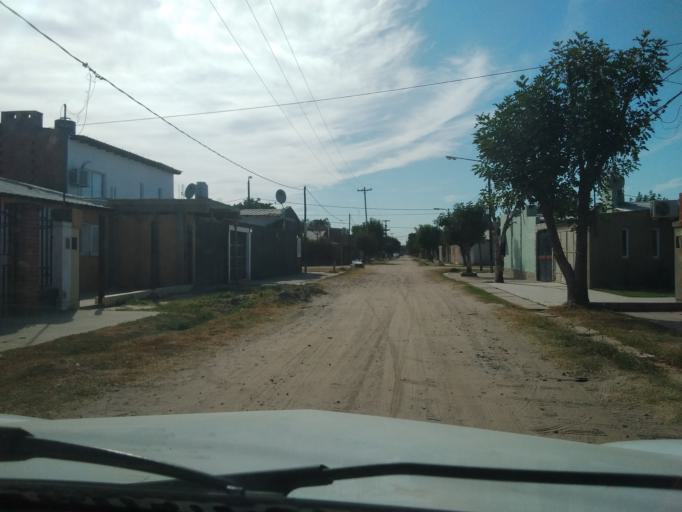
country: AR
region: Corrientes
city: Corrientes
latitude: -27.5096
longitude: -58.8038
